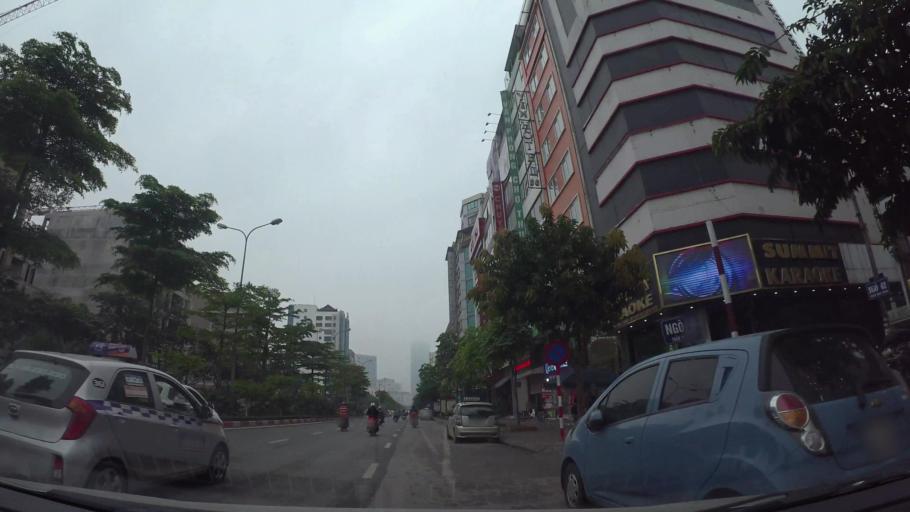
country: VN
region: Ha Noi
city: Cau Giay
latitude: 21.0342
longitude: 105.7889
